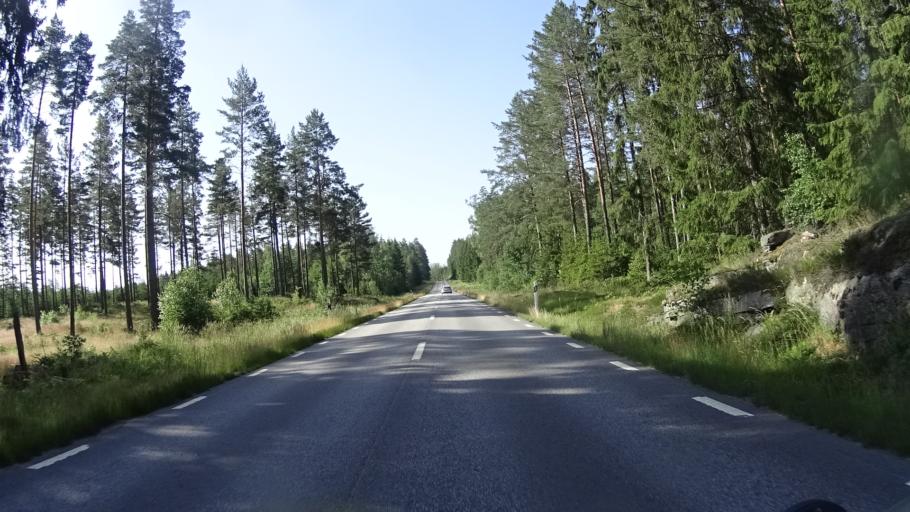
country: SE
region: OEstergoetland
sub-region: Atvidabergs Kommun
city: Atvidaberg
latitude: 58.1277
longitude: 16.0931
